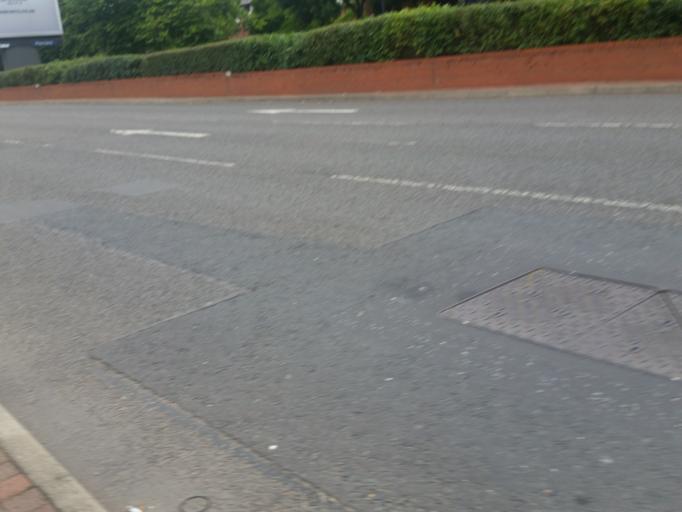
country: GB
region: England
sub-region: City and Borough of Salford
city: Salford
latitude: 53.4690
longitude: -2.2829
